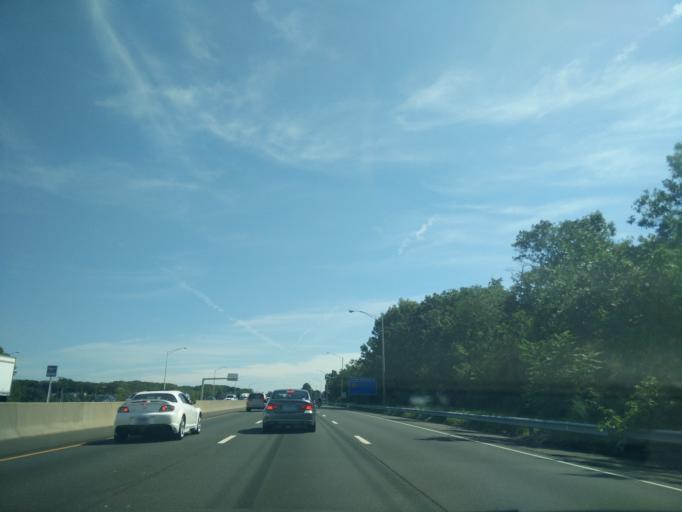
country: US
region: Connecticut
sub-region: New Haven County
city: Woodmont
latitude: 41.2371
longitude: -73.0250
